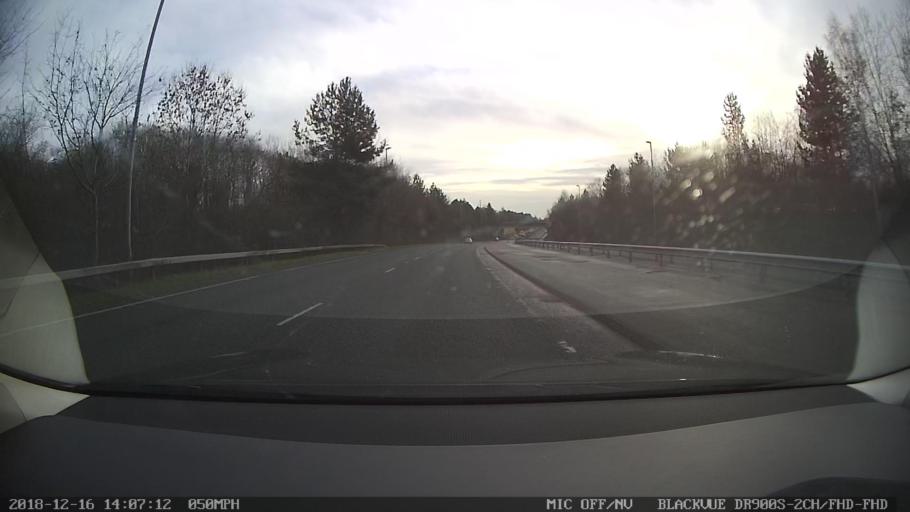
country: GB
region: England
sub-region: Borough of Stockport
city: Cheadle Hulme
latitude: 53.3750
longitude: -2.2116
